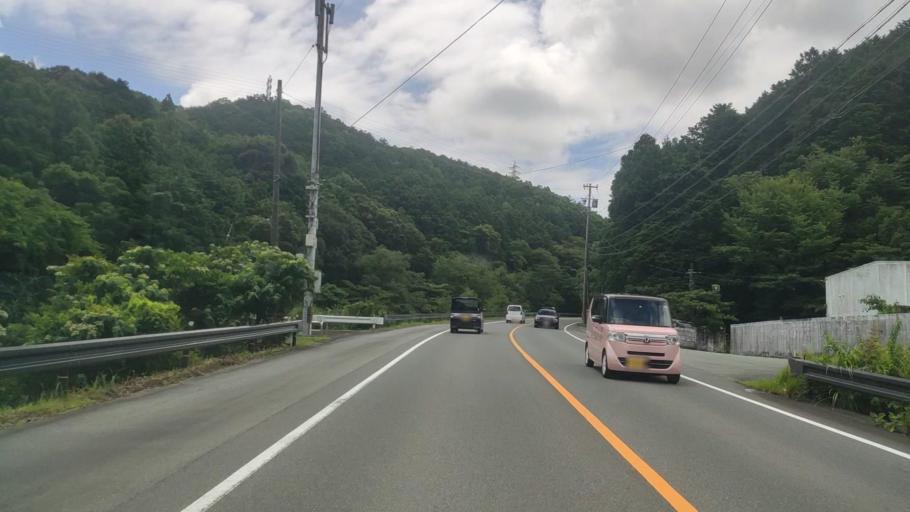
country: JP
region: Mie
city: Toba
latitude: 34.4149
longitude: 136.8162
